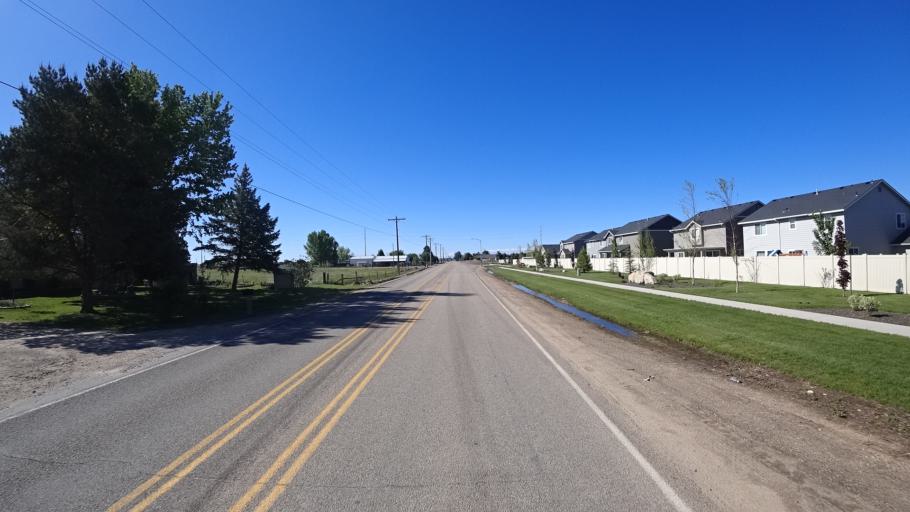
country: US
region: Idaho
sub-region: Ada County
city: Star
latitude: 43.6516
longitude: -116.4536
